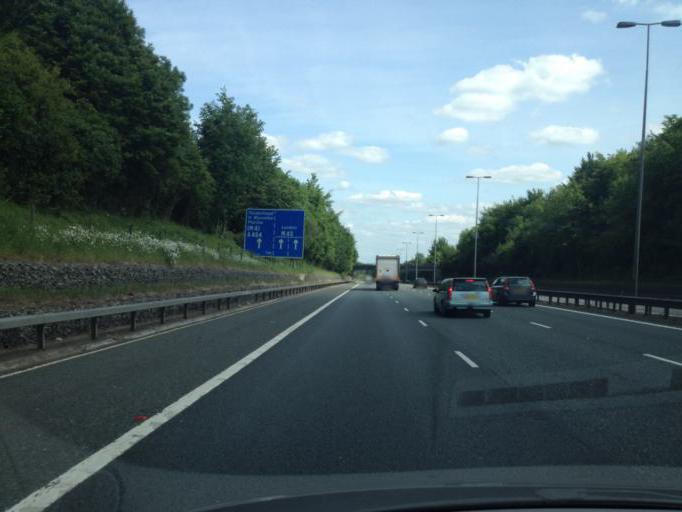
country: GB
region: England
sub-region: Buckinghamshire
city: Marlow
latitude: 51.6140
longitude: -0.8000
